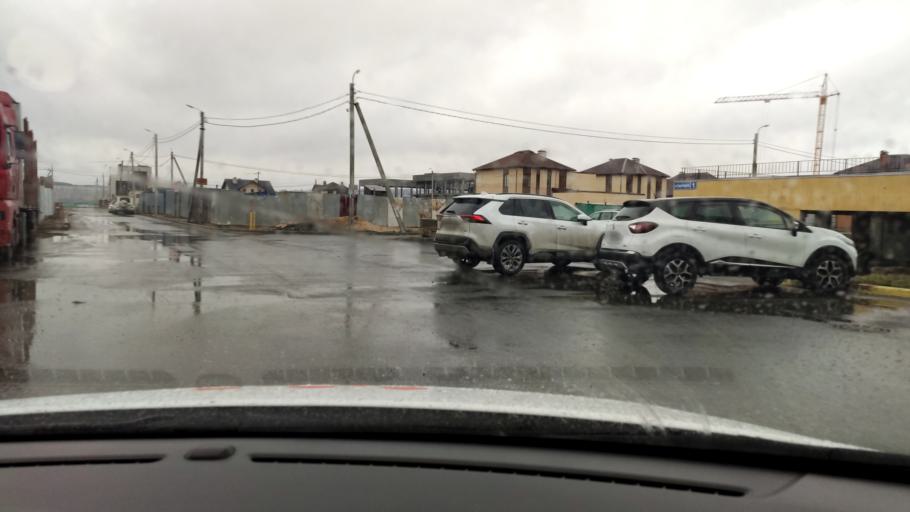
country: RU
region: Tatarstan
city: Staroye Arakchino
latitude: 55.7997
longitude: 48.9605
